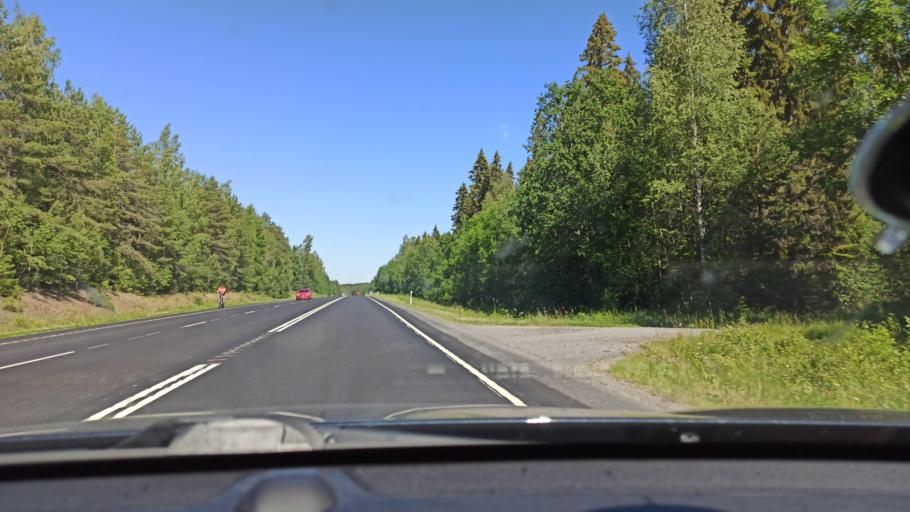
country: FI
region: Ostrobothnia
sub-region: Vaasa
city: Oravais
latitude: 63.2749
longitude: 22.3287
